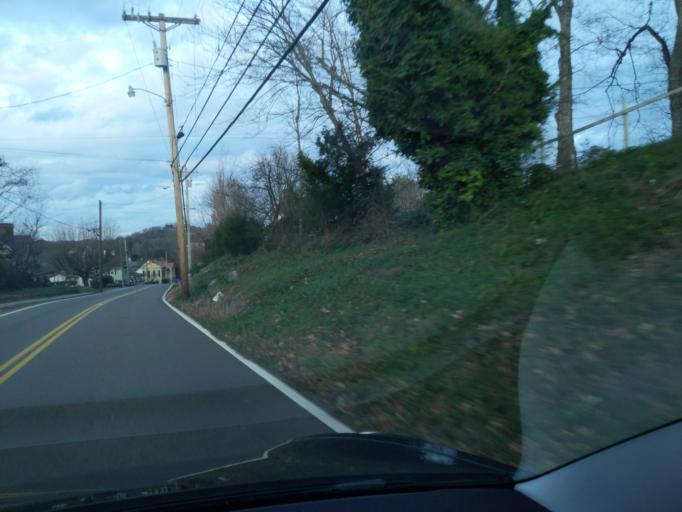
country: US
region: Tennessee
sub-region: Jefferson County
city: Dandridge
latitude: 36.0144
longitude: -83.4181
